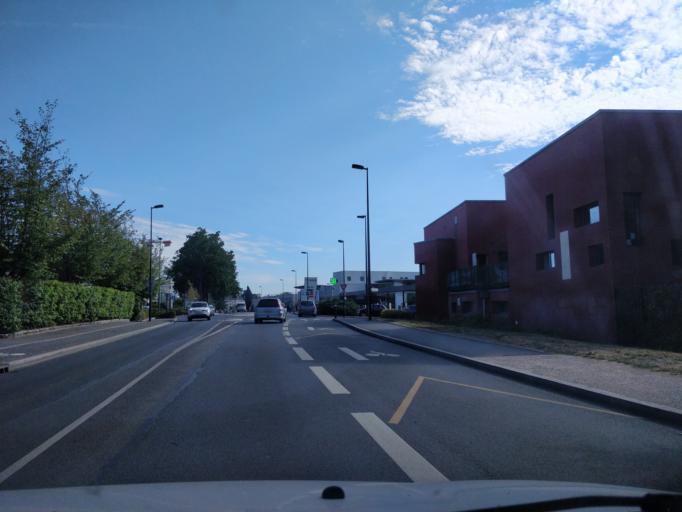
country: FR
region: Pays de la Loire
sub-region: Departement de la Loire-Atlantique
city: Nantes
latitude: 47.2456
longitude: -1.5330
